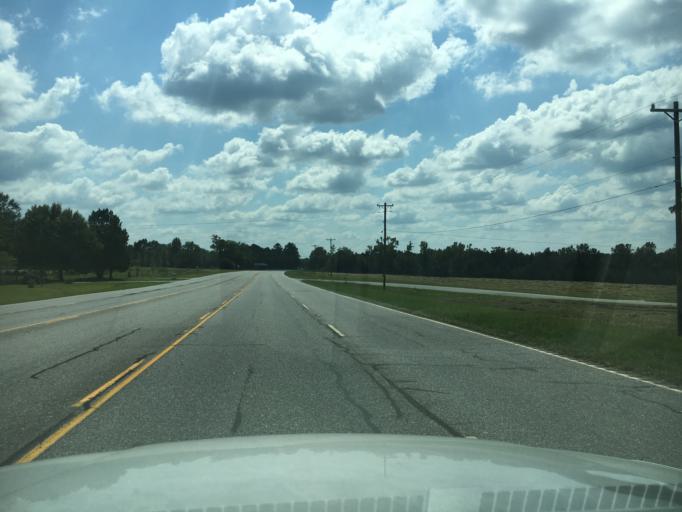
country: US
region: South Carolina
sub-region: Greenwood County
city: Ware Shoals
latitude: 34.4510
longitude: -82.2511
